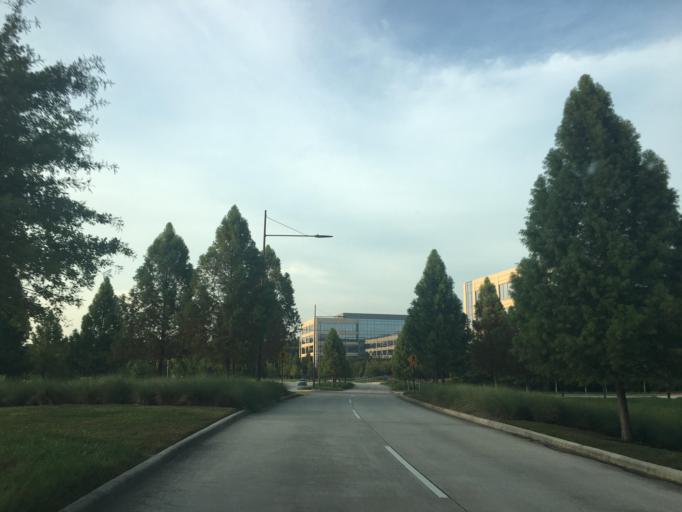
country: US
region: Texas
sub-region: Harris County
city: Spring
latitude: 30.1016
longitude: -95.4387
